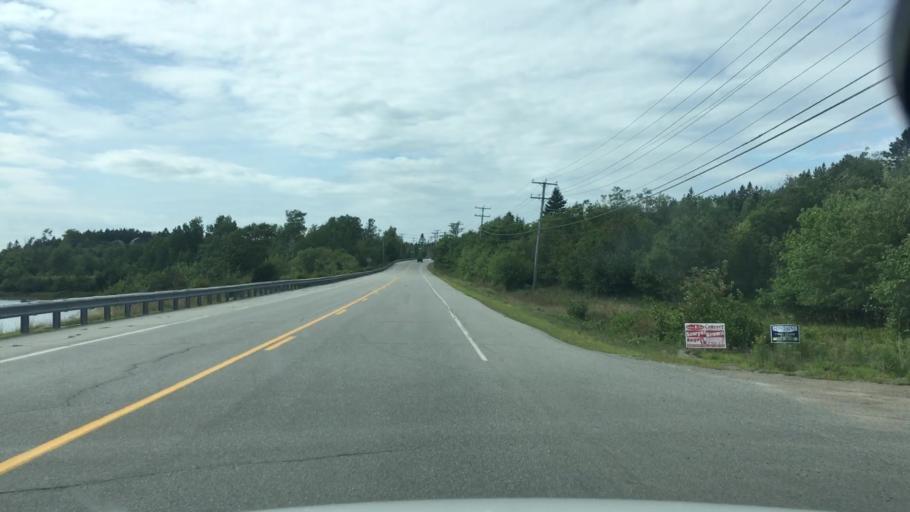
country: US
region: Maine
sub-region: Washington County
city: Eastport
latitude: 44.9255
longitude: -67.0184
